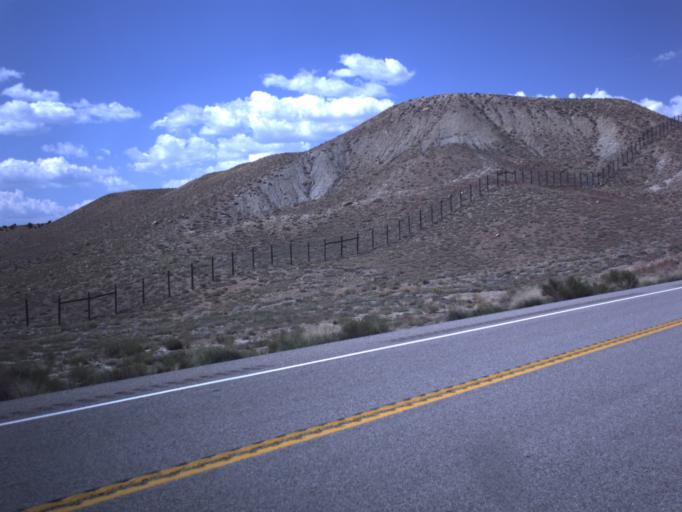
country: US
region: Utah
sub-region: Carbon County
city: Price
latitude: 39.4652
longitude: -110.8583
